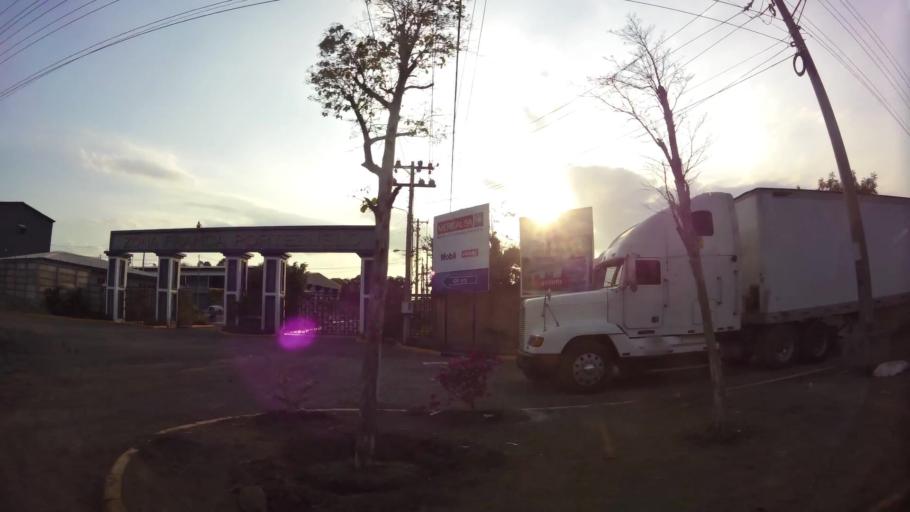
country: NI
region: Managua
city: Managua
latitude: 12.1616
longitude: -86.2238
